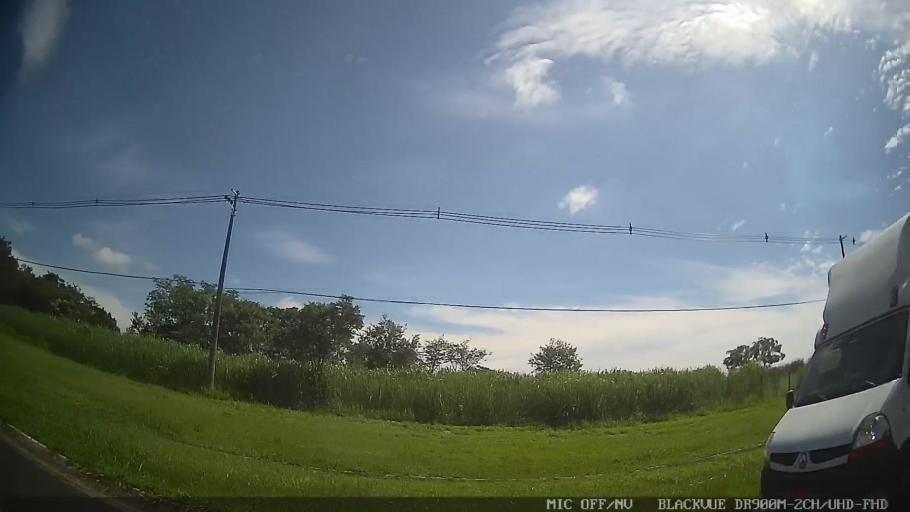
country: BR
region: Sao Paulo
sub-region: Porto Feliz
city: Porto Feliz
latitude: -23.2109
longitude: -47.5800
